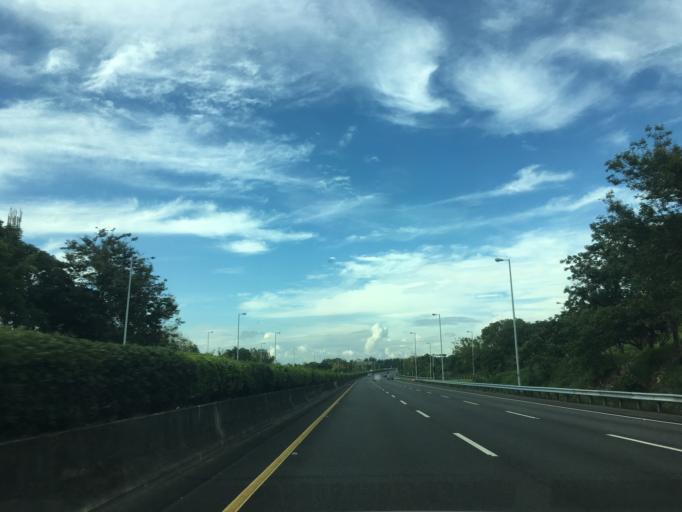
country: TW
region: Taiwan
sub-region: Yunlin
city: Douliu
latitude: 23.5966
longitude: 120.5235
